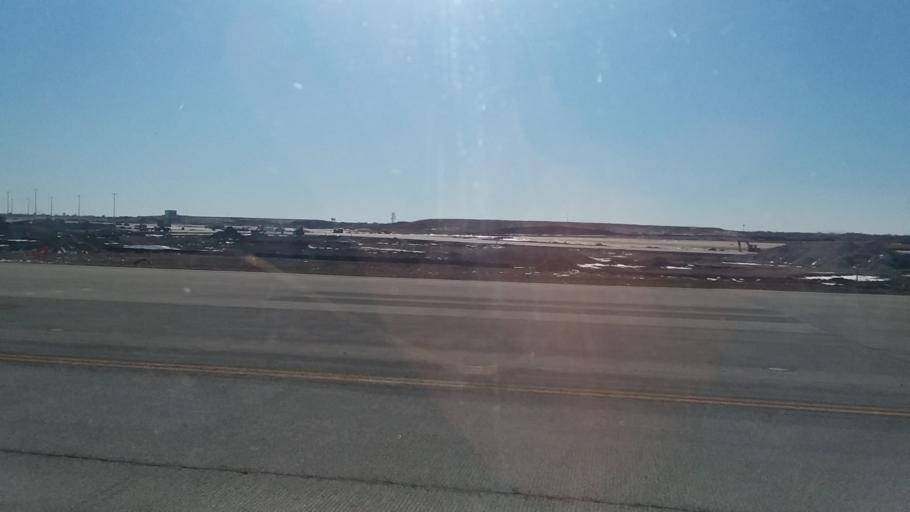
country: US
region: Illinois
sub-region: DuPage County
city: Bensenville
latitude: 41.9863
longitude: -87.9281
